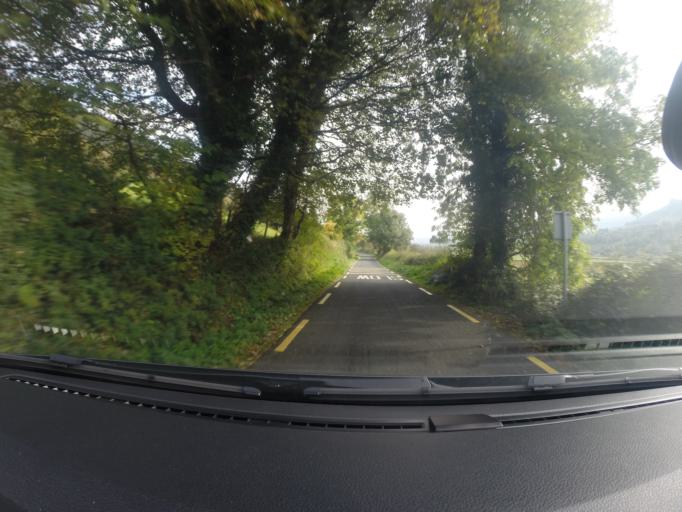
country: IE
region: Connaught
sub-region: Sligo
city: Sligo
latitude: 54.3387
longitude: -8.3669
